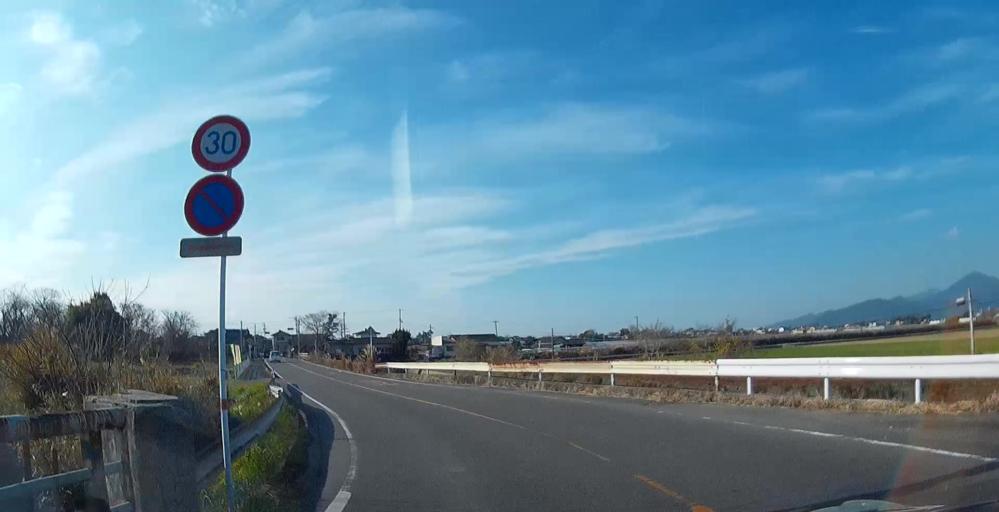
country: JP
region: Kumamoto
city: Uto
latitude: 32.7329
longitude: 130.6521
